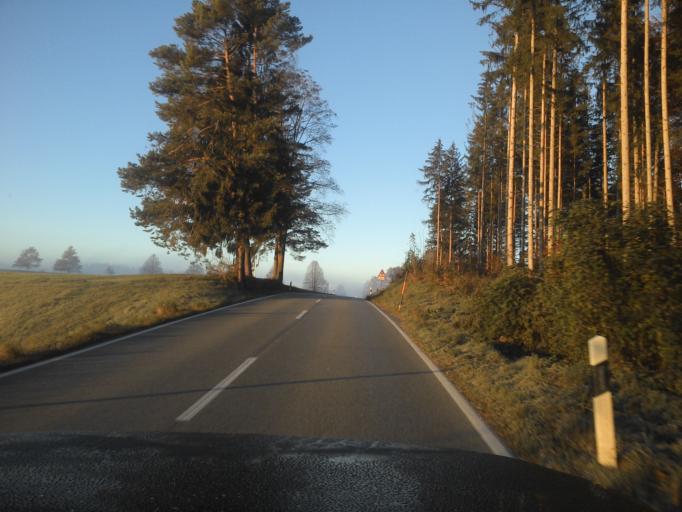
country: DE
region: Bavaria
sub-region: Upper Bavaria
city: Seeshaupt
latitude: 47.8332
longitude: 11.2592
